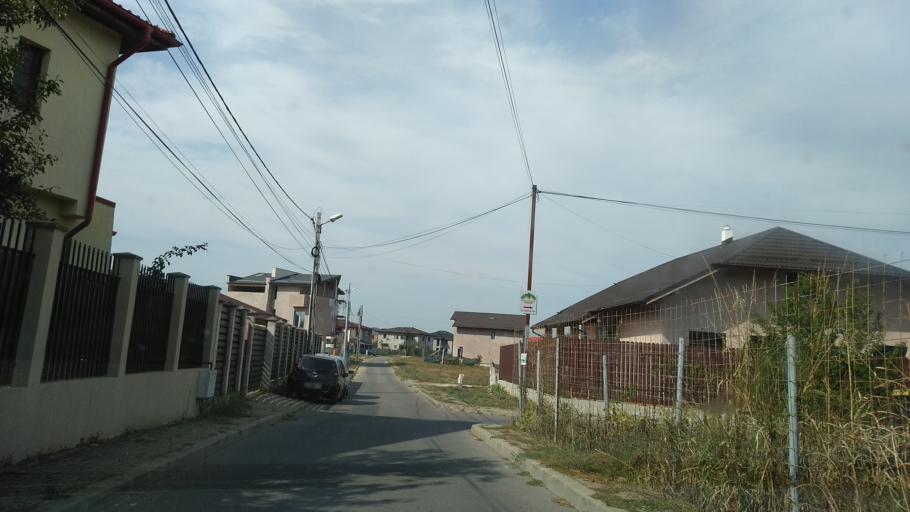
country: RO
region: Ilfov
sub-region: Comuna Chitila
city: Chitila
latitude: 44.5141
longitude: 25.9891
